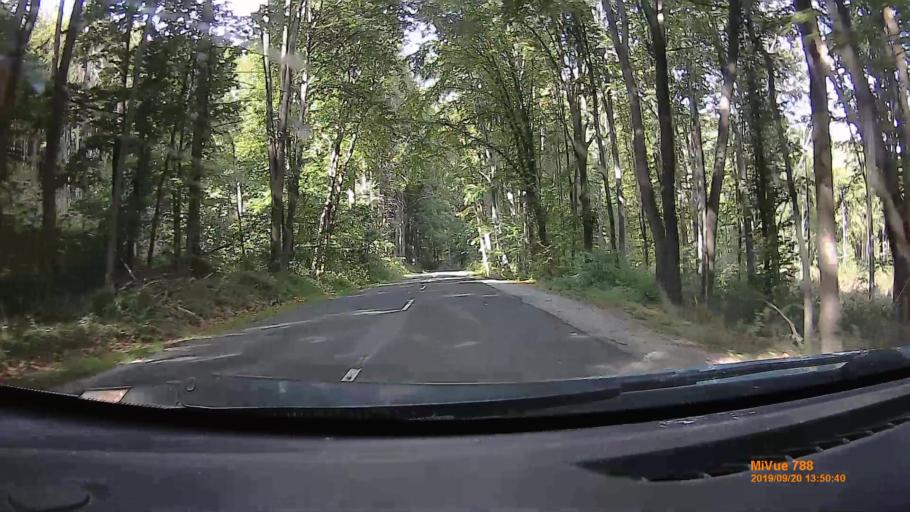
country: HU
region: Borsod-Abauj-Zemplen
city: Saly
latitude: 48.0687
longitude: 20.5894
